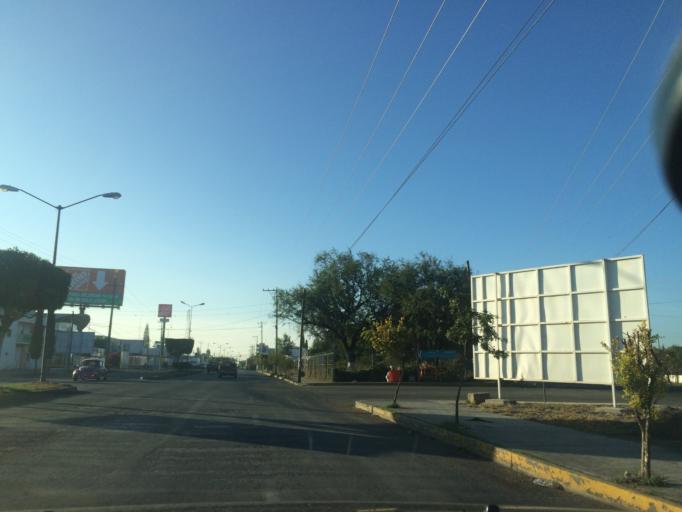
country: MX
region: Puebla
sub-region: Santiago Miahuatlan
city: San Jose Monte Chiquito
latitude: 18.4709
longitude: -97.4239
